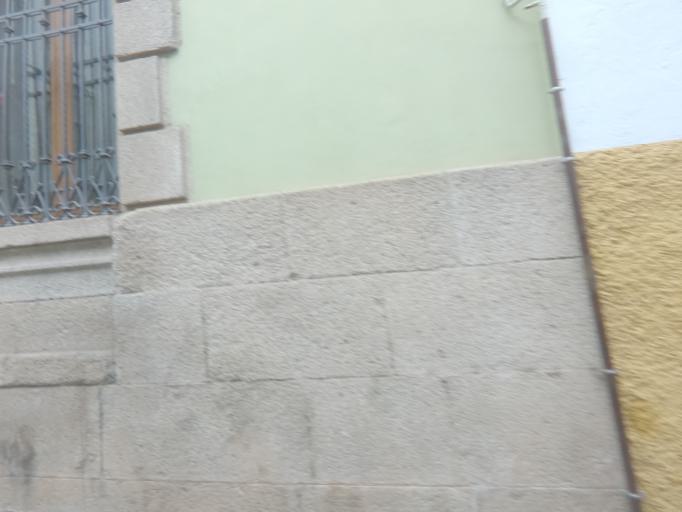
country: ES
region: Extremadura
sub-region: Provincia de Caceres
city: Caceres
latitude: 39.4764
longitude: -6.3694
